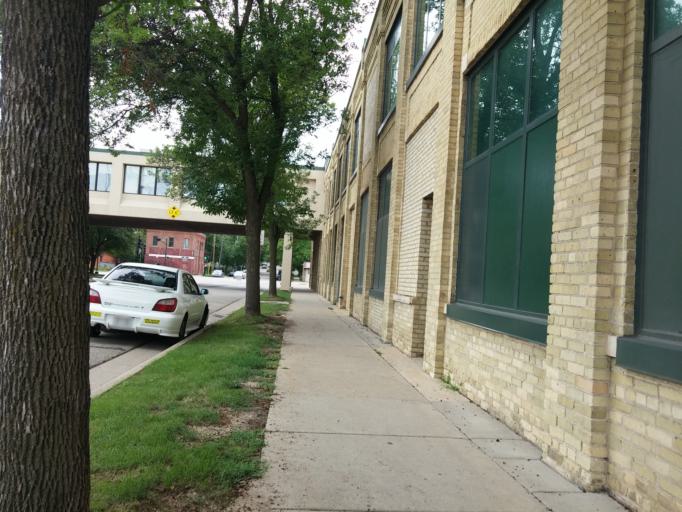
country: US
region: Wisconsin
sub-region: Dane County
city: Maple Bluff
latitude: 43.0868
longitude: -89.3655
